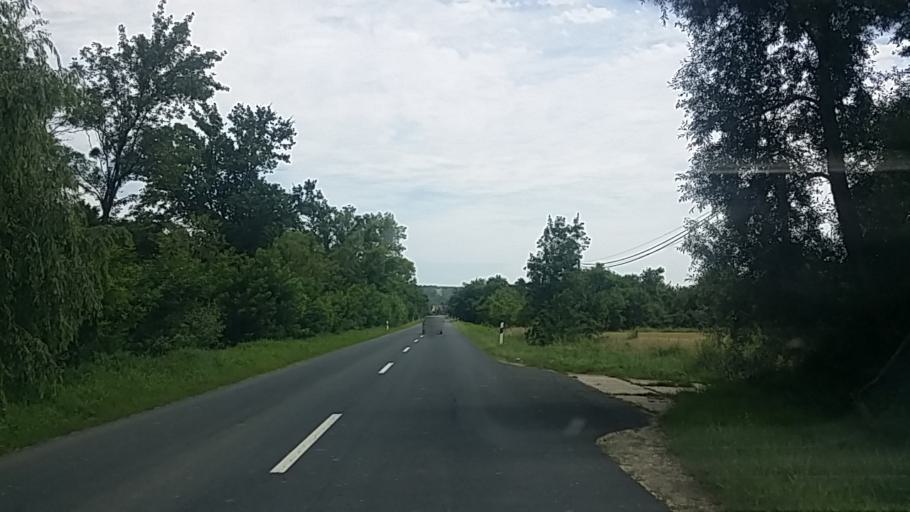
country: HR
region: Medimurska
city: Podturen
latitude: 46.5163
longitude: 16.5691
